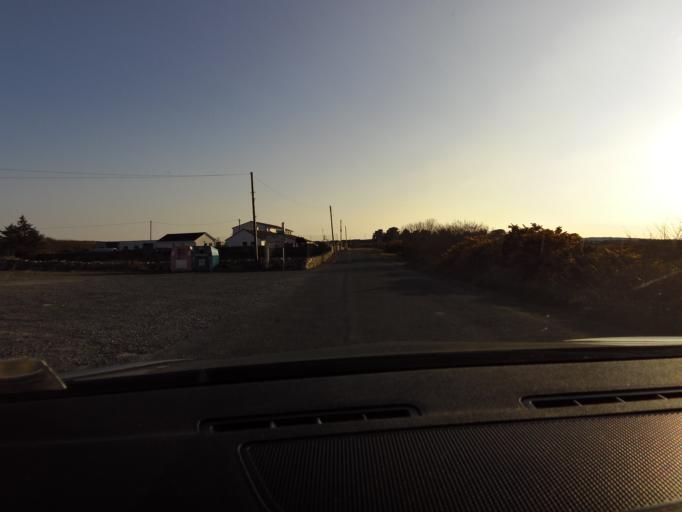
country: IE
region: Connaught
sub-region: County Galway
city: Oughterard
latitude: 53.2766
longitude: -9.5317
